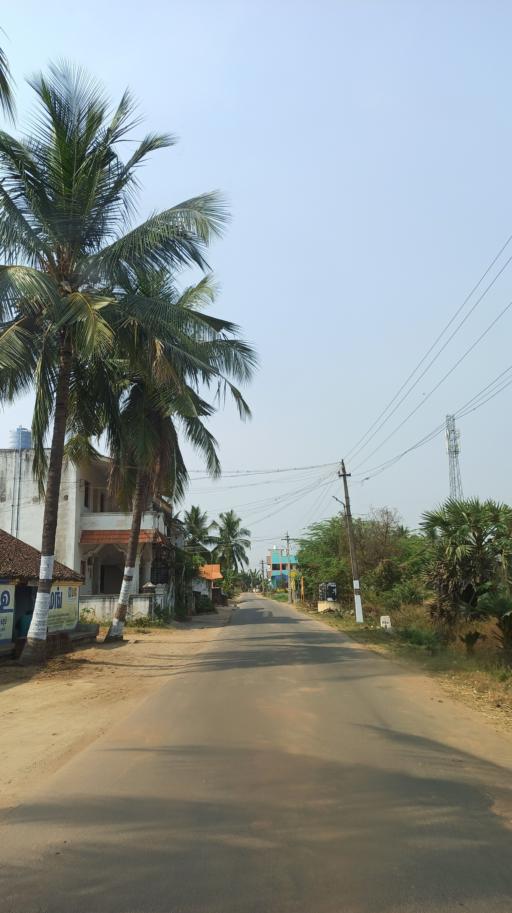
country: IN
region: Tamil Nadu
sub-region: Tiruvannamalai
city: Desur
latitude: 12.4526
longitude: 79.3727
